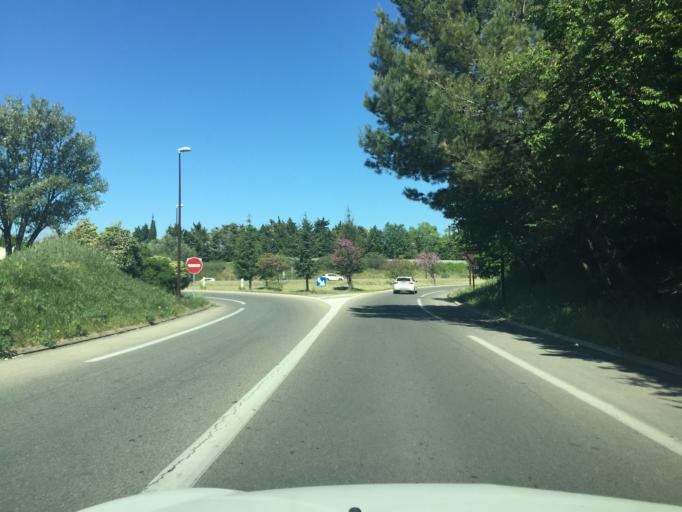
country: FR
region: Provence-Alpes-Cote d'Azur
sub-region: Departement du Vaucluse
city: Le Pontet
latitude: 43.9466
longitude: 4.8415
